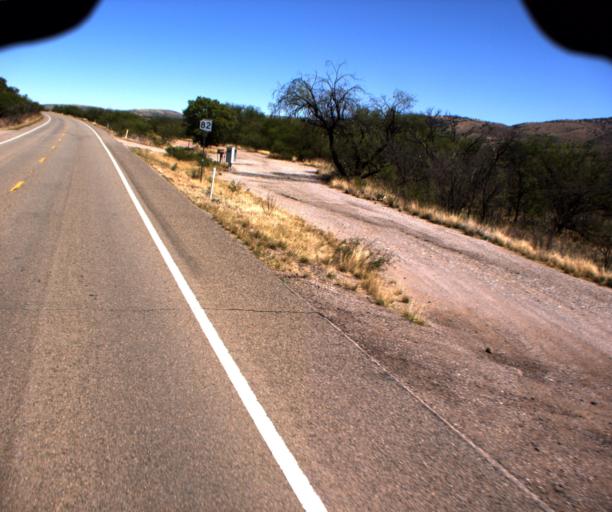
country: US
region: Arizona
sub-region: Santa Cruz County
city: Rio Rico
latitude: 31.5979
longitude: -110.7235
